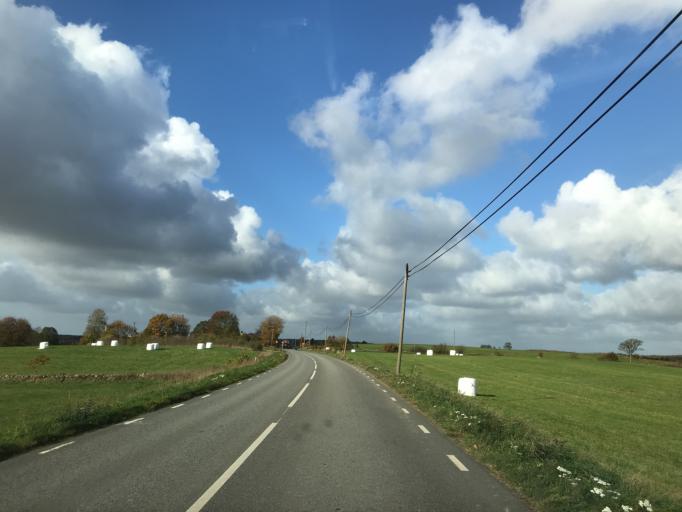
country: SE
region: Skane
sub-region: Perstorps Kommun
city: Perstorp
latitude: 56.0419
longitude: 13.3875
